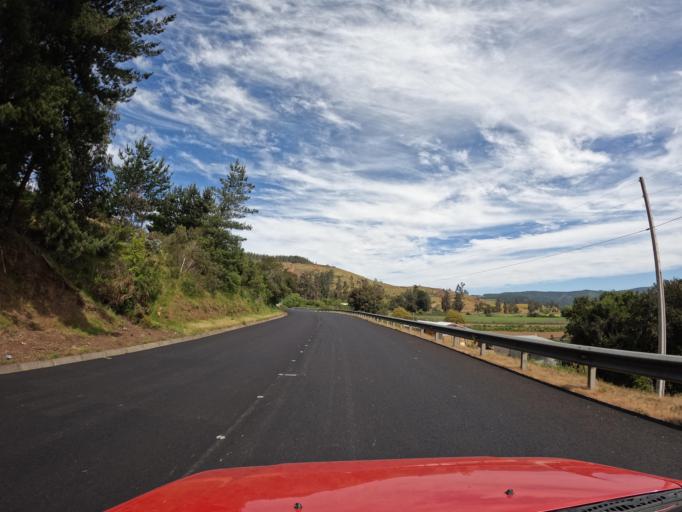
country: CL
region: Maule
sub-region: Provincia de Talca
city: Constitucion
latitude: -35.0665
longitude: -72.0386
